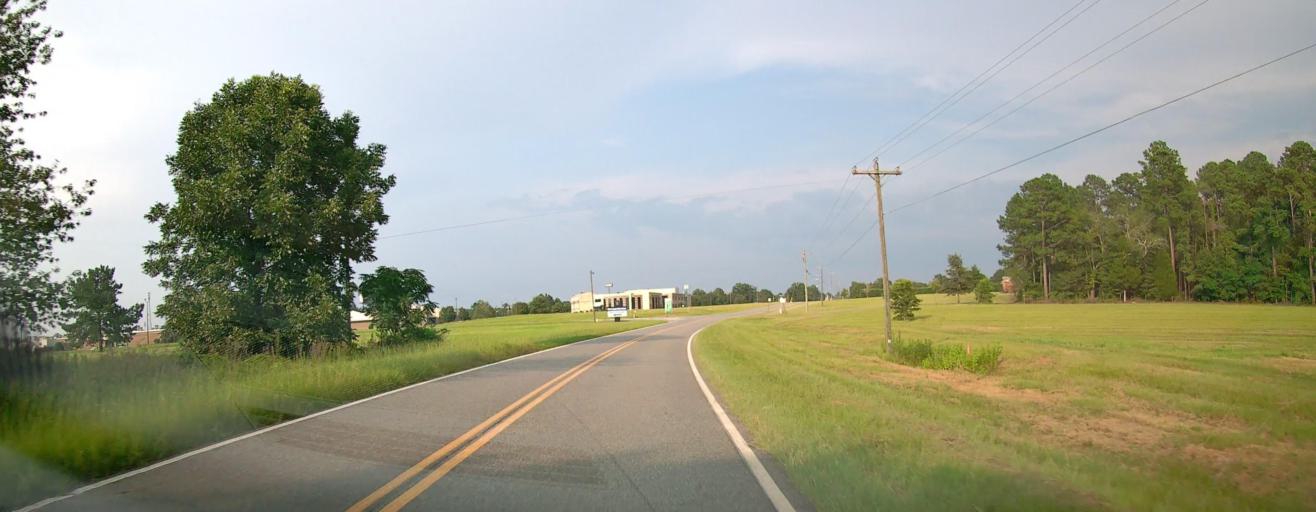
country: US
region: Georgia
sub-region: Laurens County
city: Dublin
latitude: 32.4831
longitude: -82.9474
